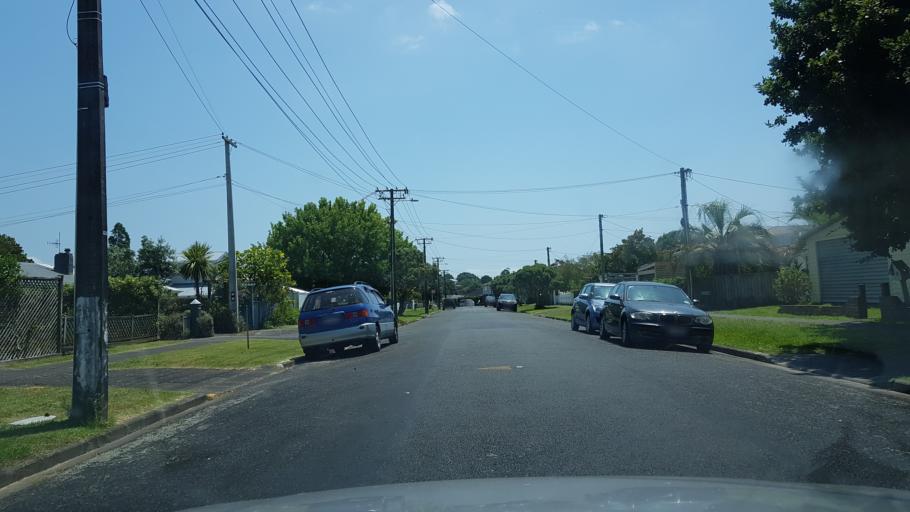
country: NZ
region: Auckland
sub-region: Auckland
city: North Shore
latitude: -36.8116
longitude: 174.7954
